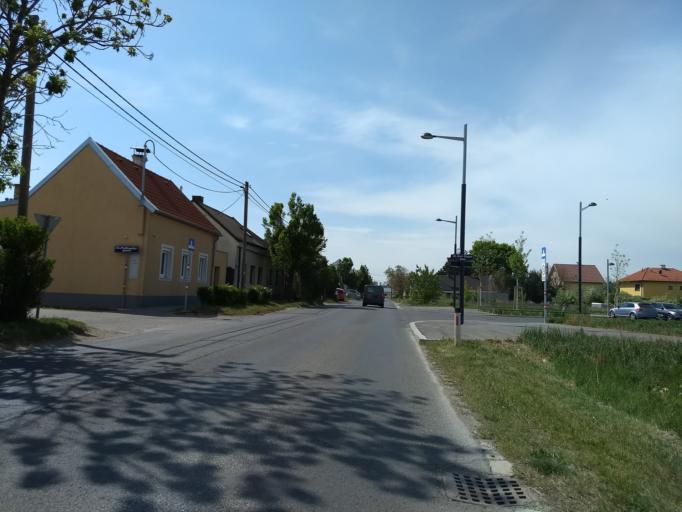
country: AT
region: Lower Austria
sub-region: Politischer Bezirk Wien-Umgebung
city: Gerasdorf bei Wien
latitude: 48.2422
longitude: 16.4923
